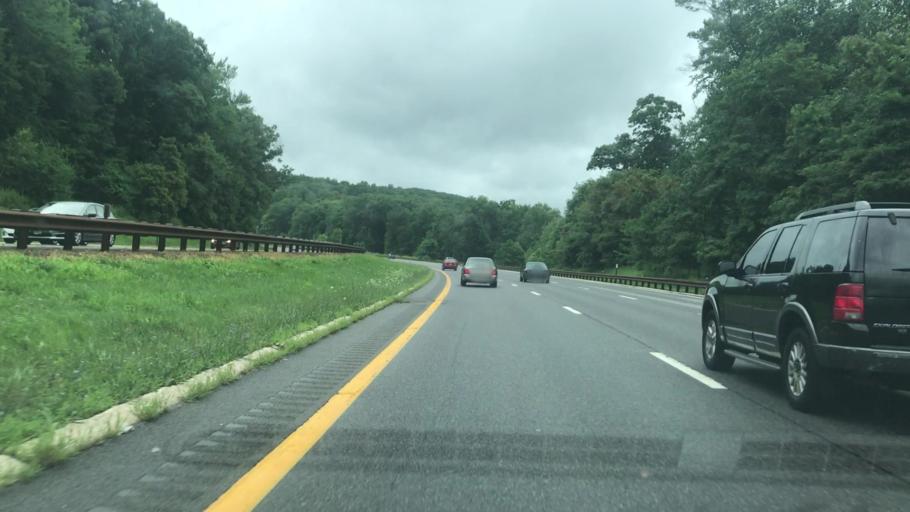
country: US
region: New York
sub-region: Westchester County
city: Shrub Oak
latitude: 41.3217
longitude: -73.8262
